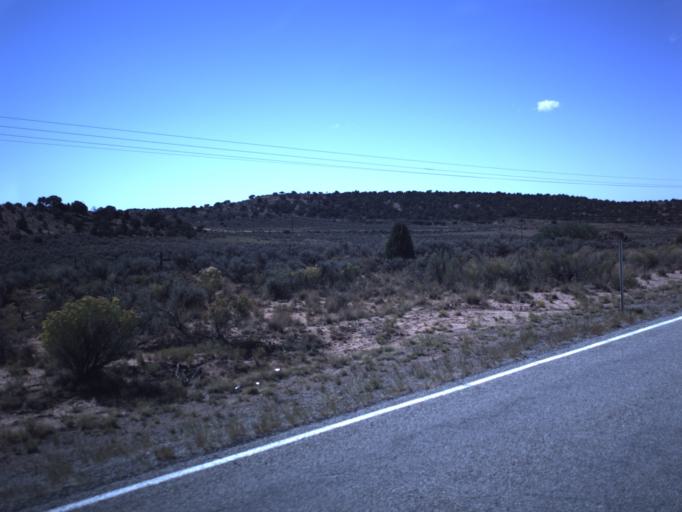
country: US
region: Utah
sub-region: Grand County
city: Moab
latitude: 38.3049
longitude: -109.3891
